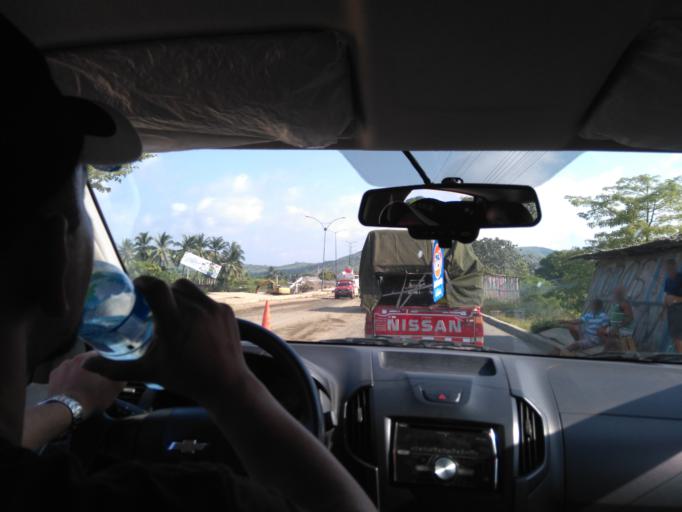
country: EC
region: Manabi
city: Portoviejo
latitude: -0.9913
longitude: -80.4690
